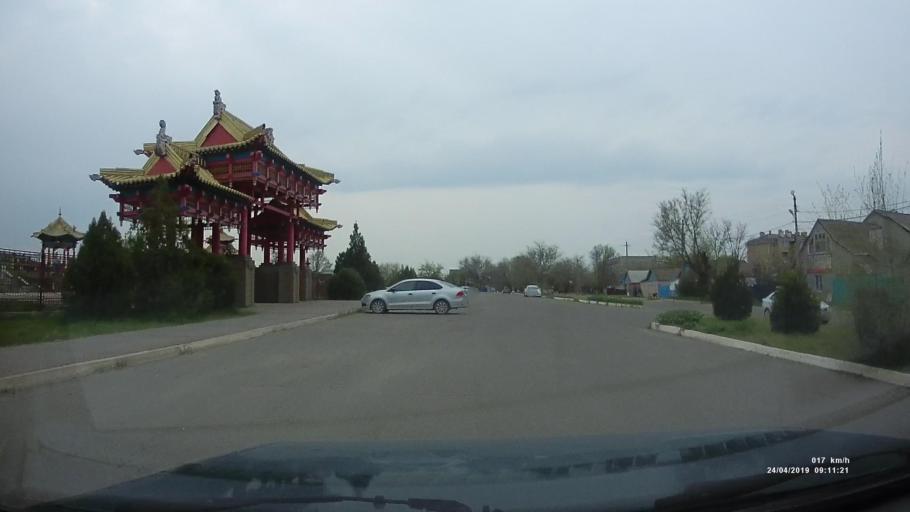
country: RU
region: Kalmykiya
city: Elista
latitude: 46.3097
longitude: 44.2823
